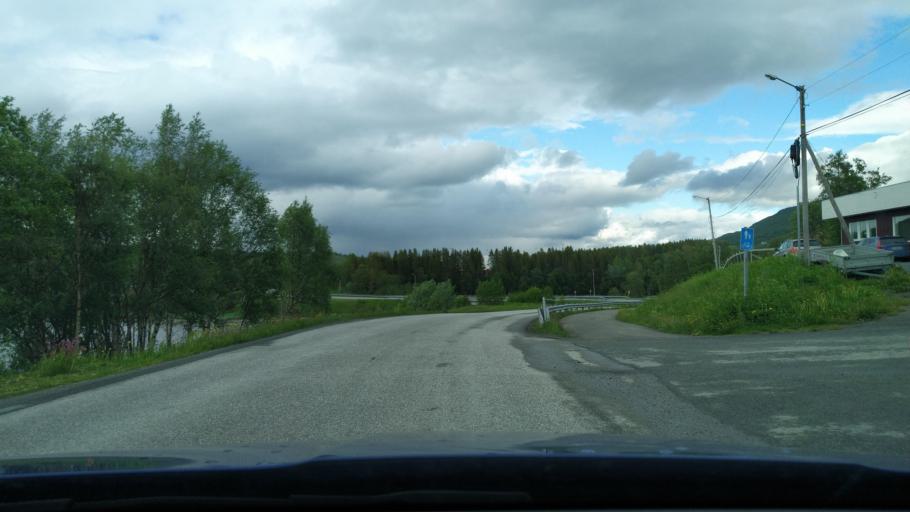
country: NO
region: Troms
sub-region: Dyroy
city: Brostadbotn
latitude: 69.0850
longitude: 17.6924
